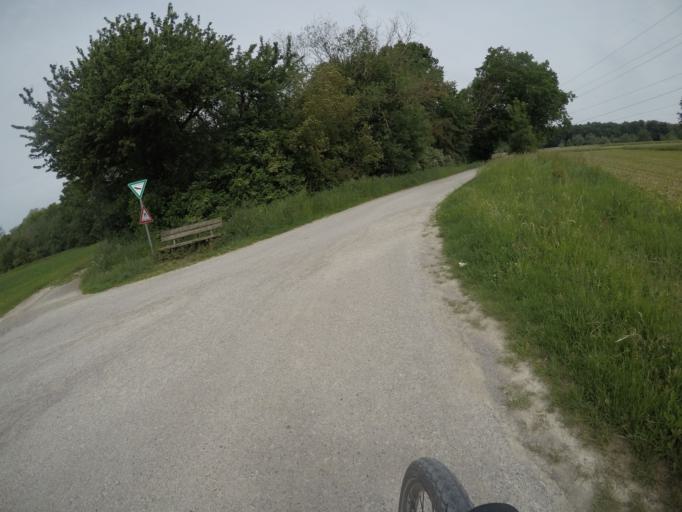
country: DE
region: Baden-Wuerttemberg
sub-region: Regierungsbezirk Stuttgart
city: Waldenbuch
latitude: 48.5905
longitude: 9.1499
